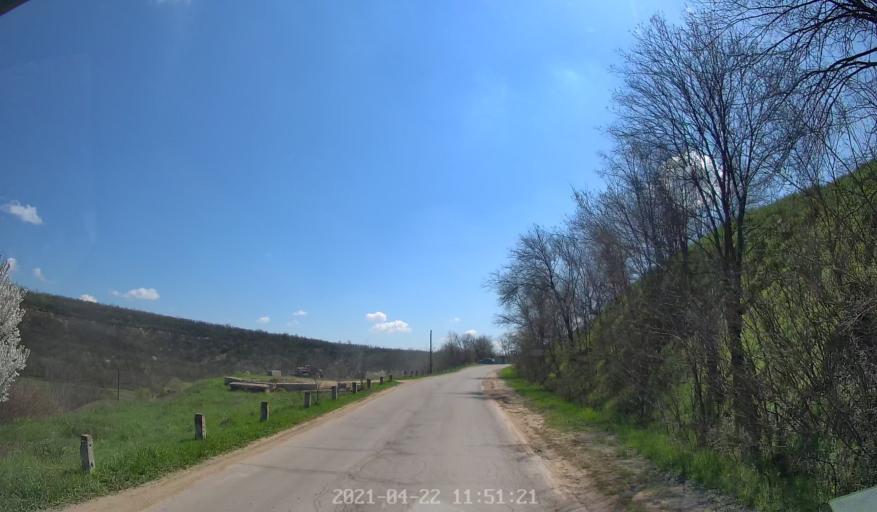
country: MD
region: Chisinau
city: Ciorescu
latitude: 47.1363
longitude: 28.9085
